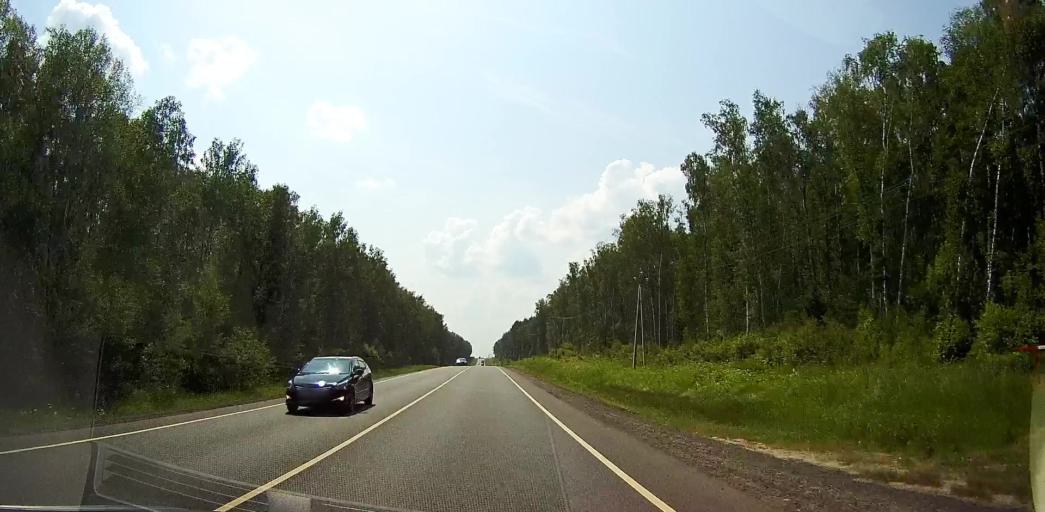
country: RU
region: Moskovskaya
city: Meshcherino
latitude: 55.1655
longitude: 38.3209
